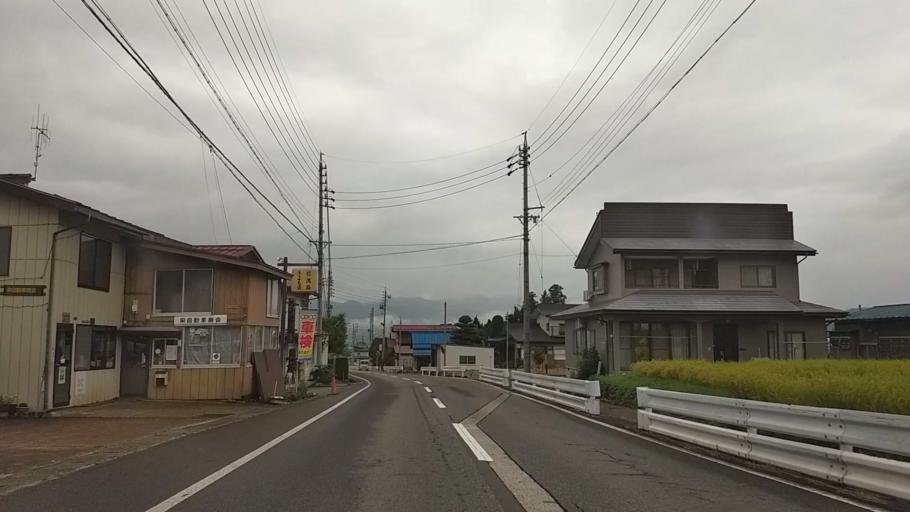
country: JP
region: Nagano
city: Iiyama
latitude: 36.8396
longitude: 138.4077
